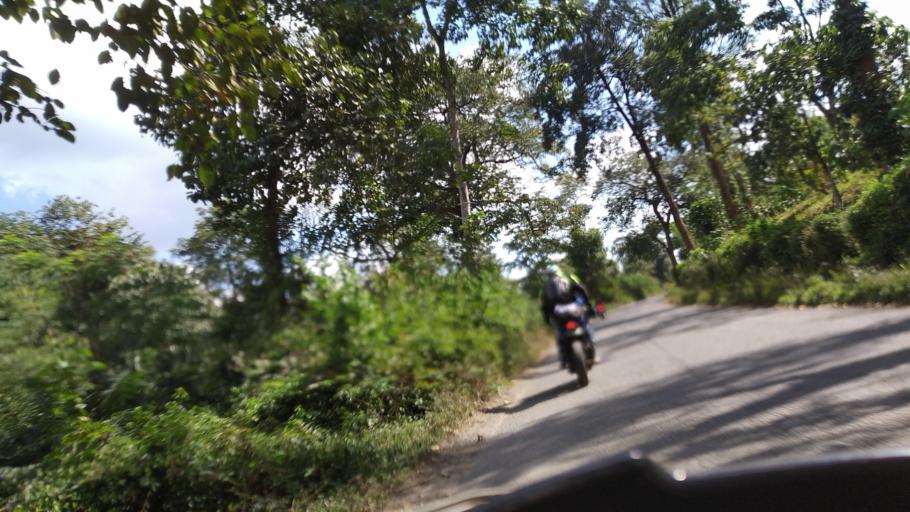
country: IN
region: Karnataka
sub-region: Kodagu
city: Ponnampet
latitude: 11.9598
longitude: 76.0621
